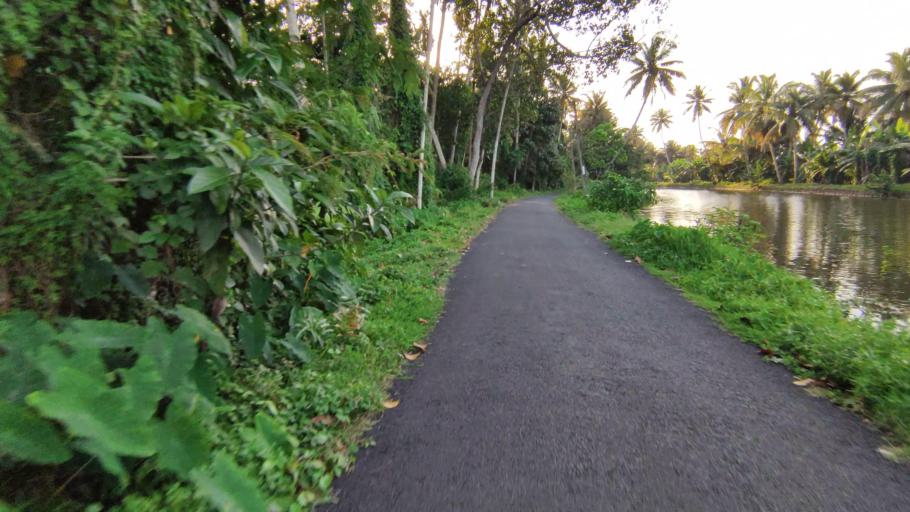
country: IN
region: Kerala
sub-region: Kottayam
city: Kottayam
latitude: 9.5767
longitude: 76.4452
